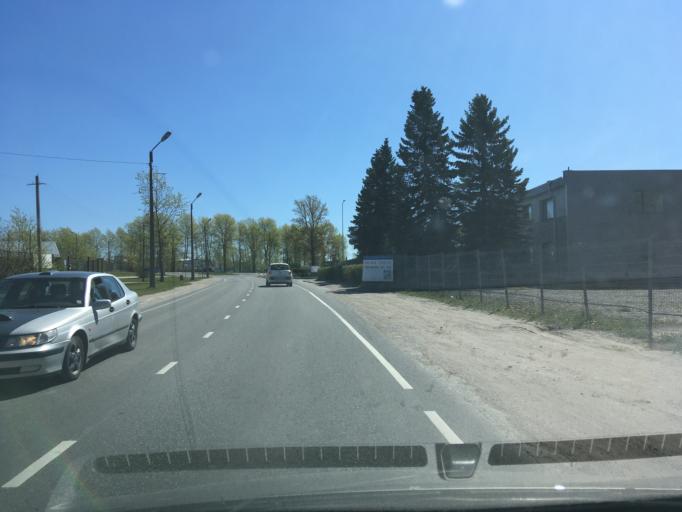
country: EE
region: Harju
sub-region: Maardu linn
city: Maardu
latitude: 59.4558
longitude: 24.9973
